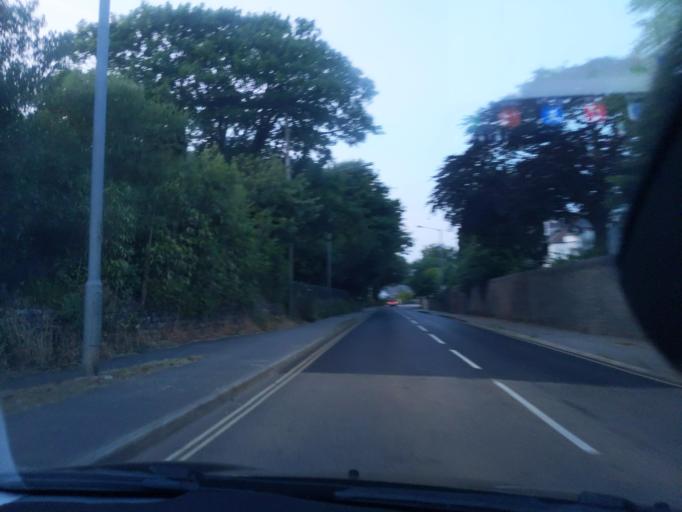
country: GB
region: England
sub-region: Cornwall
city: Camborne
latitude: 50.2081
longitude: -5.3047
